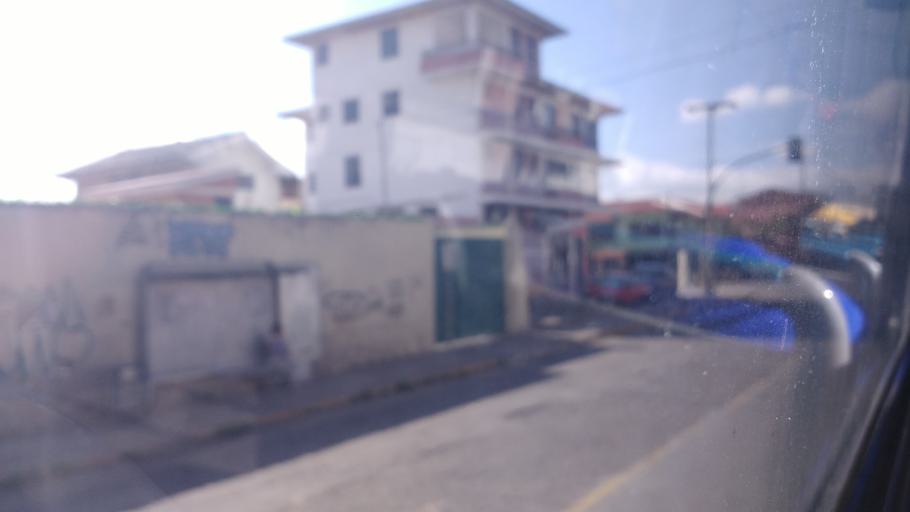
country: EC
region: Azuay
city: Cuenca
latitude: -2.8954
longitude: -79.0233
